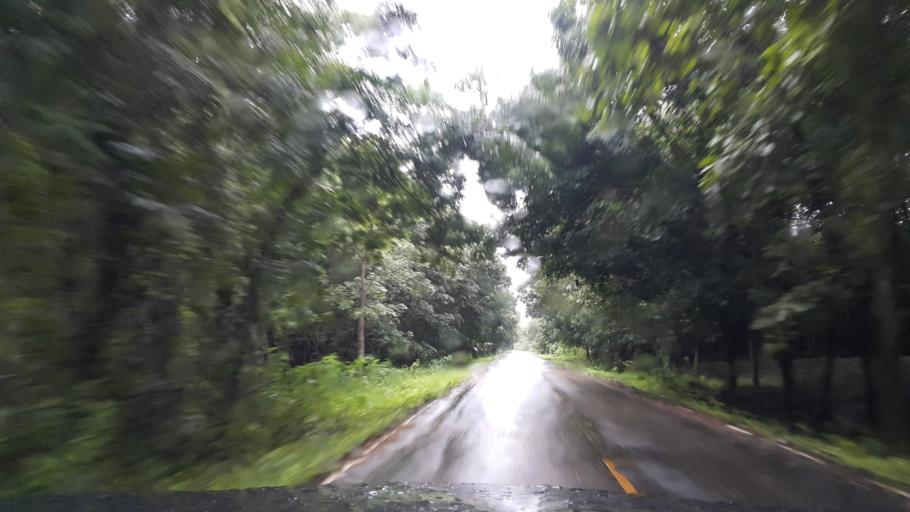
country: TH
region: Phayao
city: Phu Sang
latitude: 19.6140
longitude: 100.4072
